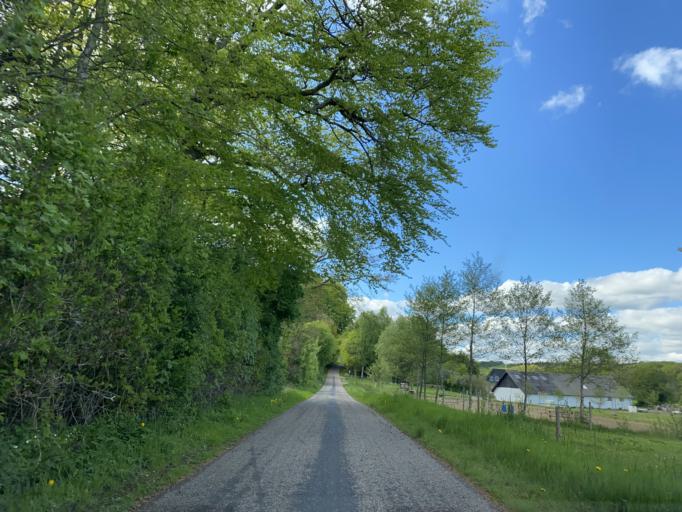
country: DK
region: Central Jutland
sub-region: Skanderborg Kommune
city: Galten
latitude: 56.1650
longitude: 9.8534
